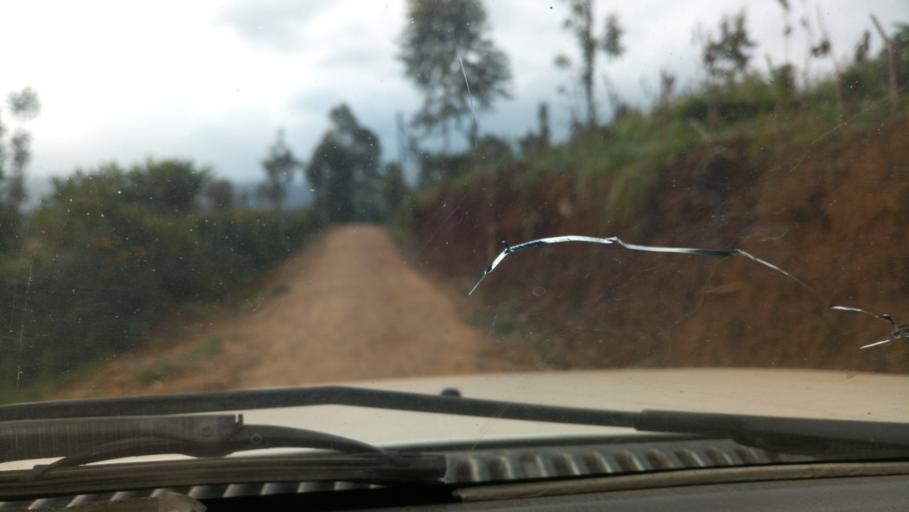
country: KE
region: Murang'a District
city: Kangema
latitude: -0.7055
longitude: 36.9491
